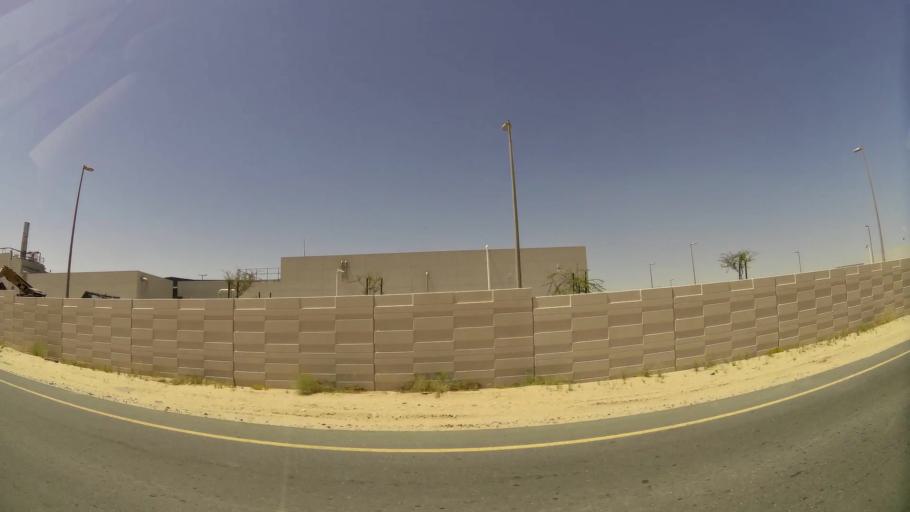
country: AE
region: Dubai
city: Dubai
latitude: 24.9770
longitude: 55.1954
